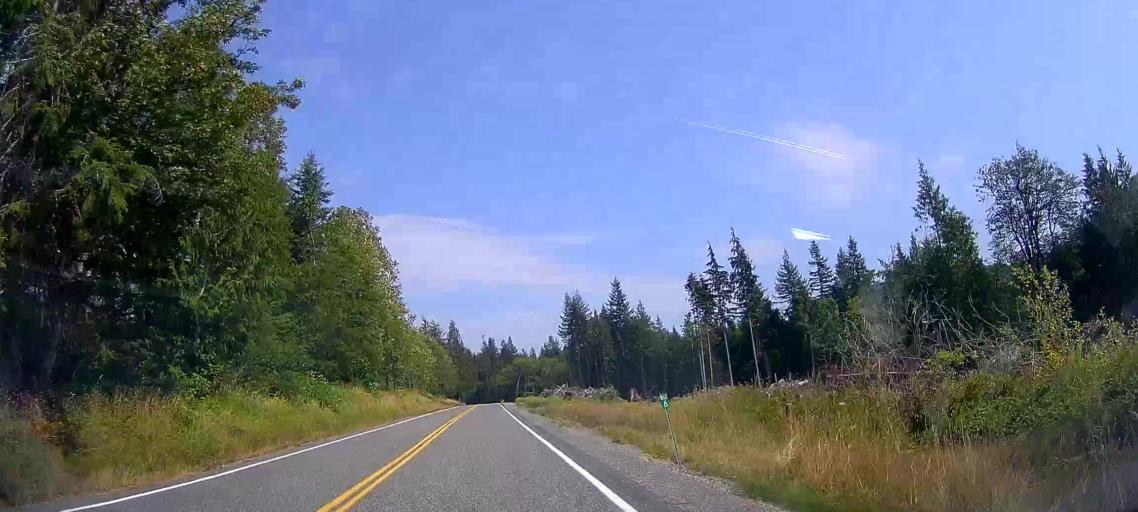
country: US
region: Washington
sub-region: Snohomish County
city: Bryant
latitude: 48.3395
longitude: -122.1166
